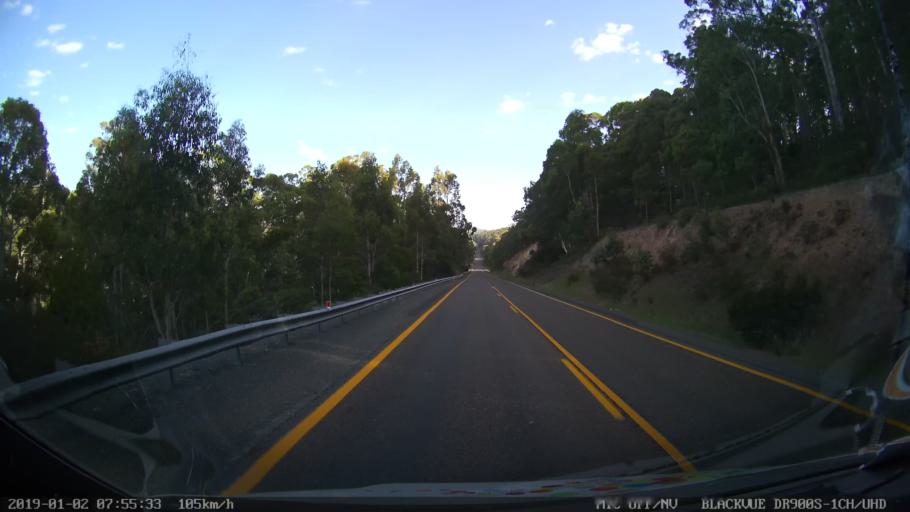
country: AU
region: New South Wales
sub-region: Tumut Shire
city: Tumut
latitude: -35.6832
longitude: 148.4867
